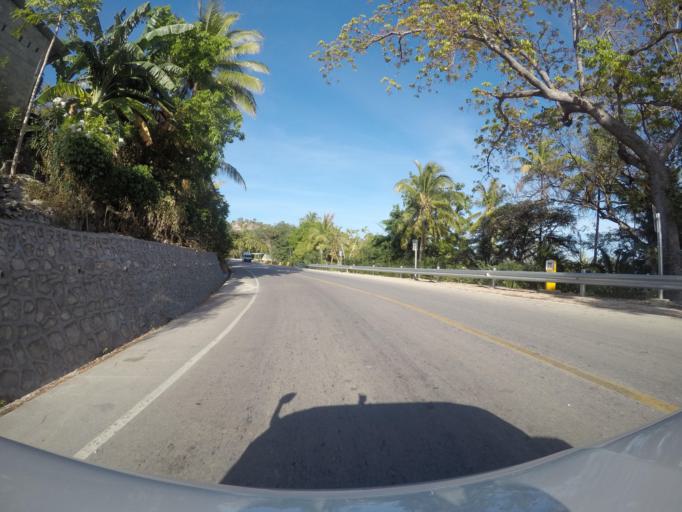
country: TL
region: Baucau
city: Baucau
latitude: -8.4571
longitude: 126.4659
